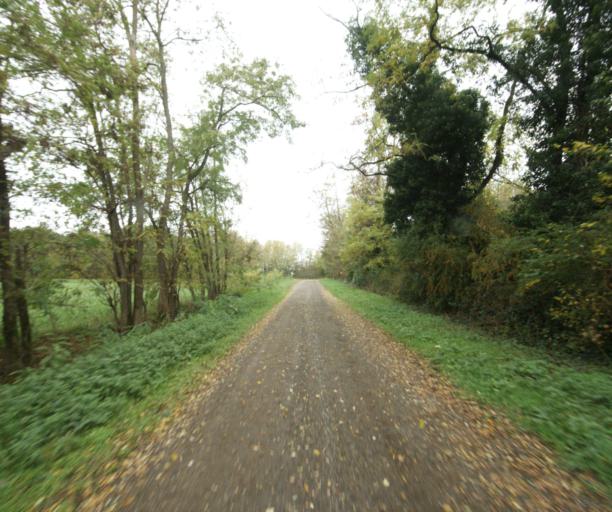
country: FR
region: Rhone-Alpes
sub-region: Departement de l'Ain
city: Pont-de-Vaux
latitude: 46.4620
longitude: 4.8965
